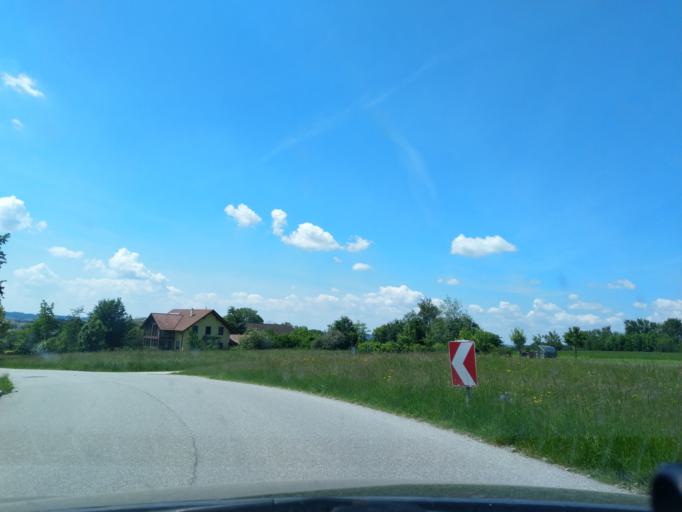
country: AT
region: Upper Austria
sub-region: Politischer Bezirk Ried im Innkreis
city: Ried im Innkreis
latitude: 48.2079
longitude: 13.5420
